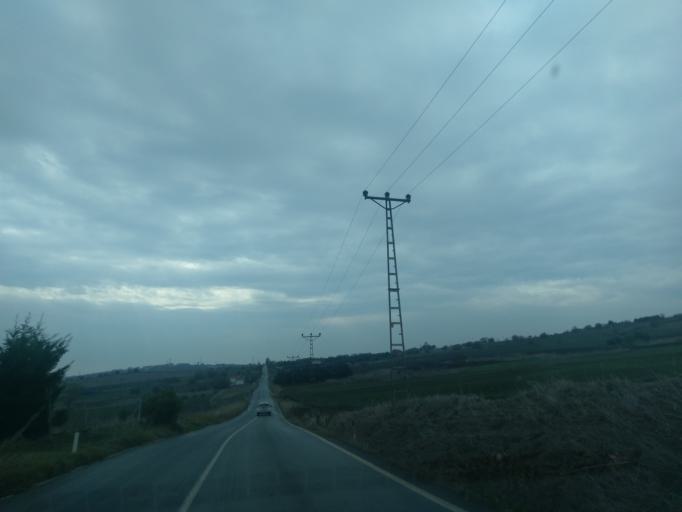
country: TR
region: Istanbul
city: Canta
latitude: 41.1073
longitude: 28.0796
